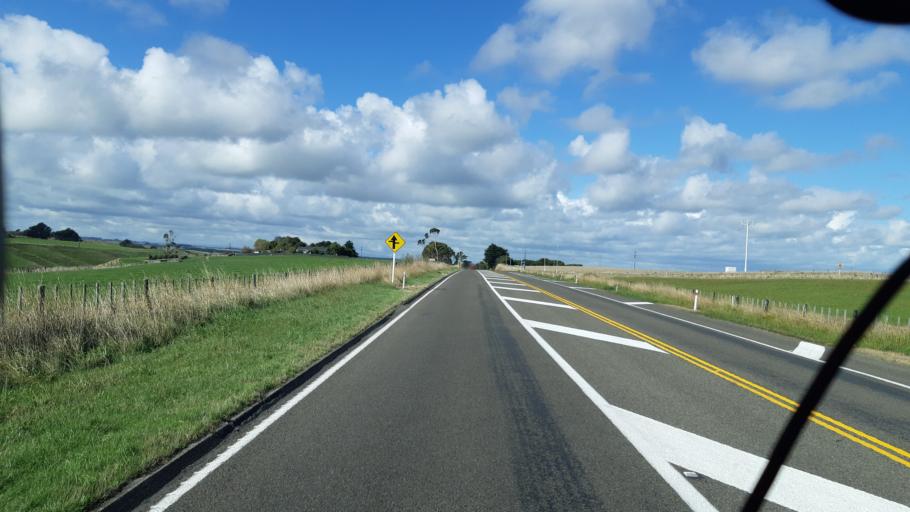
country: NZ
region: Manawatu-Wanganui
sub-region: Wanganui District
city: Wanganui
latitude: -40.0265
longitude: 175.1912
